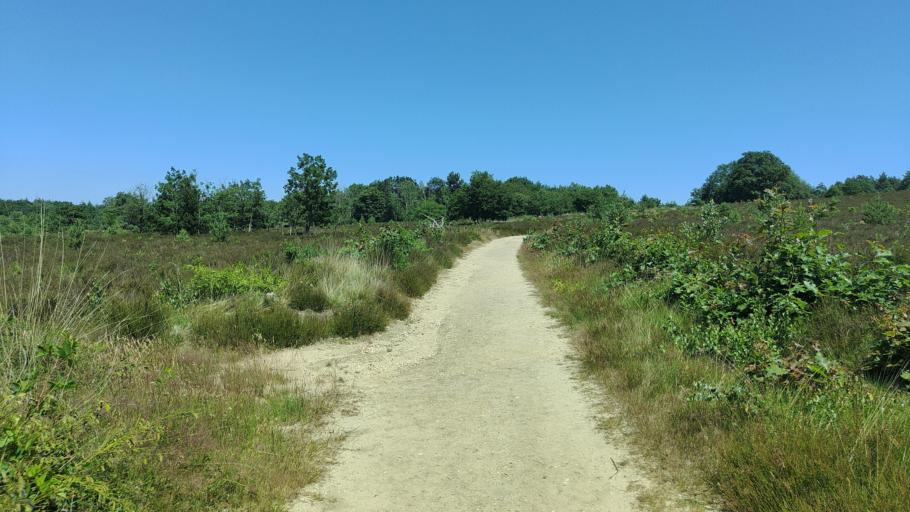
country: NL
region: North Brabant
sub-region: Gemeente Cuijk
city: Cuijk
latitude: 51.7731
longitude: 5.8853
